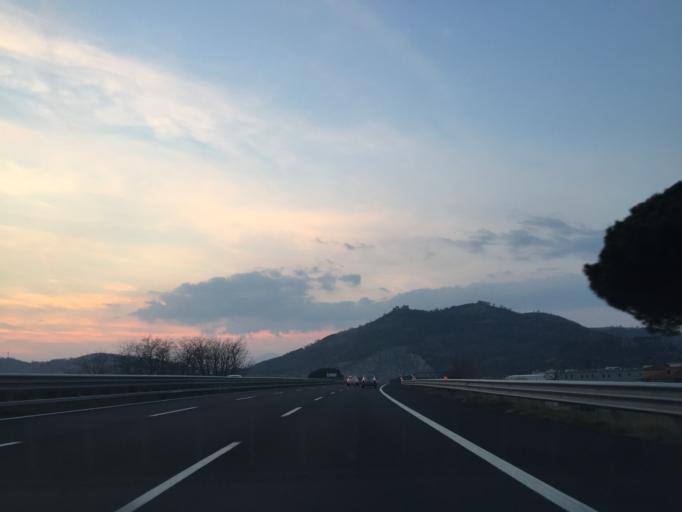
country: IT
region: Campania
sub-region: Provincia di Salerno
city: Casali-San Potito
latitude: 40.7681
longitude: 14.6756
